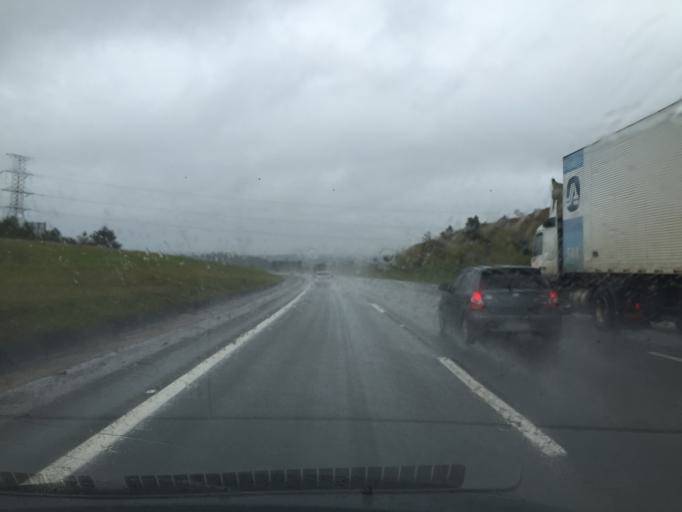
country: BR
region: Sao Paulo
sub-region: Mairinque
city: Mairinque
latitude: -23.4235
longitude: -47.2417
